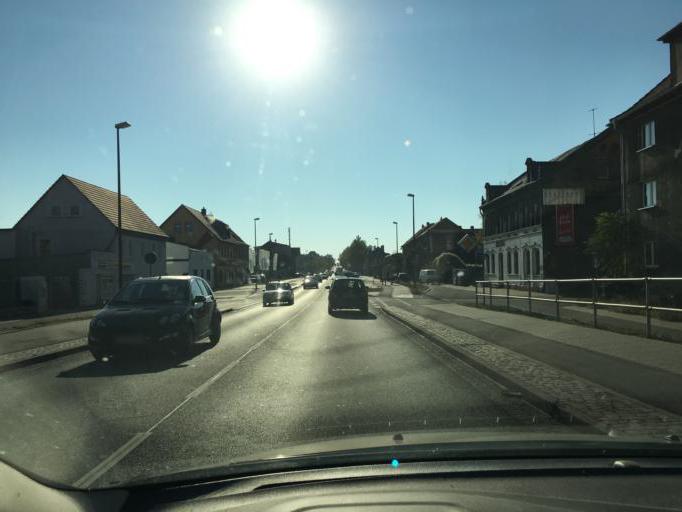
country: DE
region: Saxony
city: Bitterfeld-Wolfen
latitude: 51.6155
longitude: 12.3126
